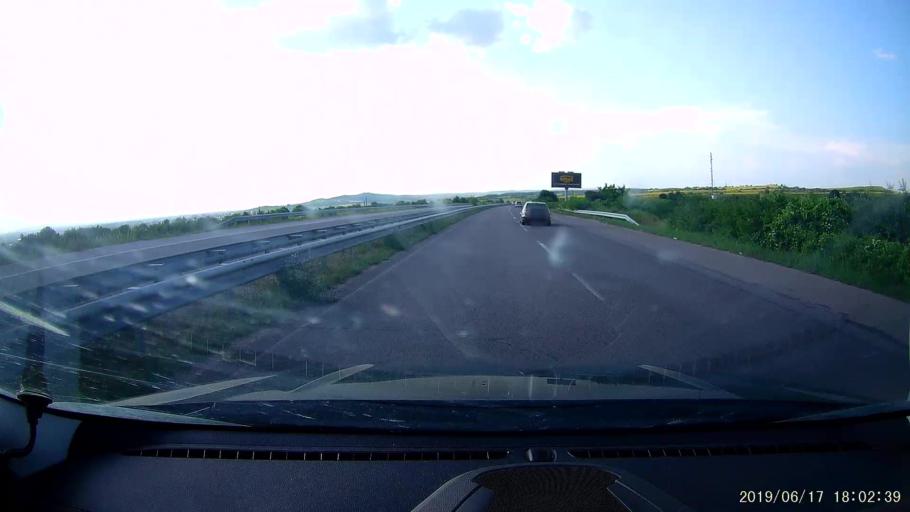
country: BG
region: Khaskovo
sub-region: Obshtina Svilengrad
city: Svilengrad
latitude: 41.7635
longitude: 26.2279
